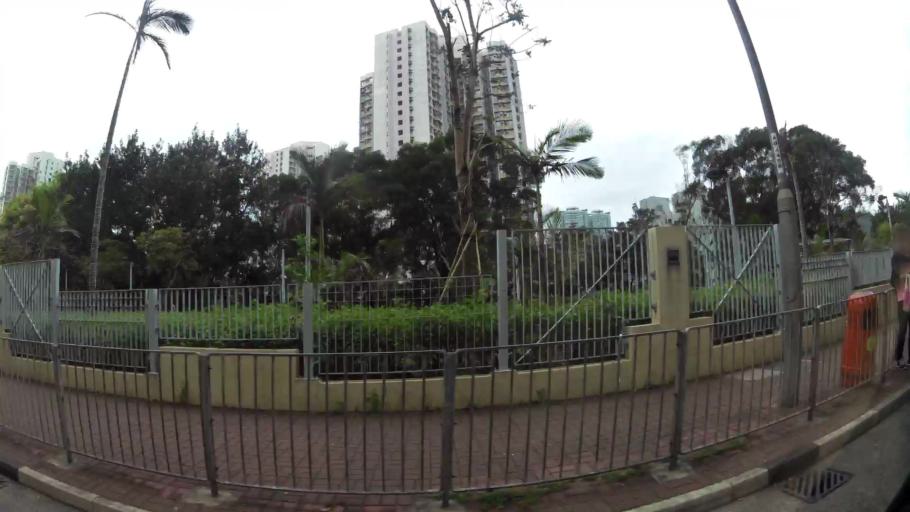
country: HK
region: Kowloon City
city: Kowloon
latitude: 22.3225
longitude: 114.2297
